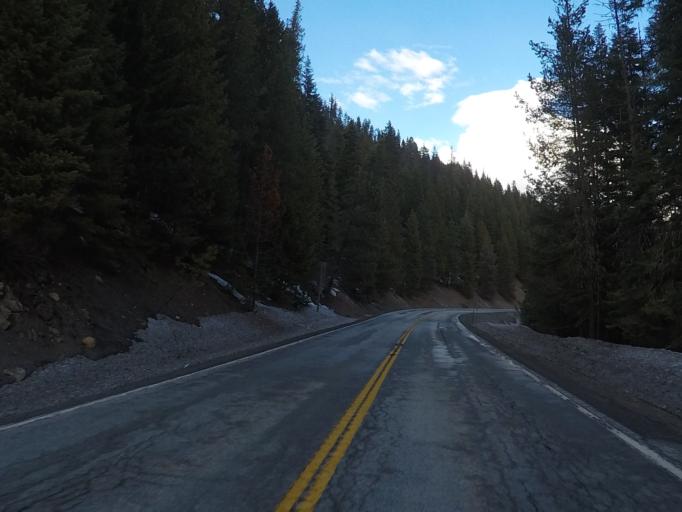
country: US
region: Montana
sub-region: Ravalli County
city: Hamilton
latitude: 46.5142
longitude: -114.7274
